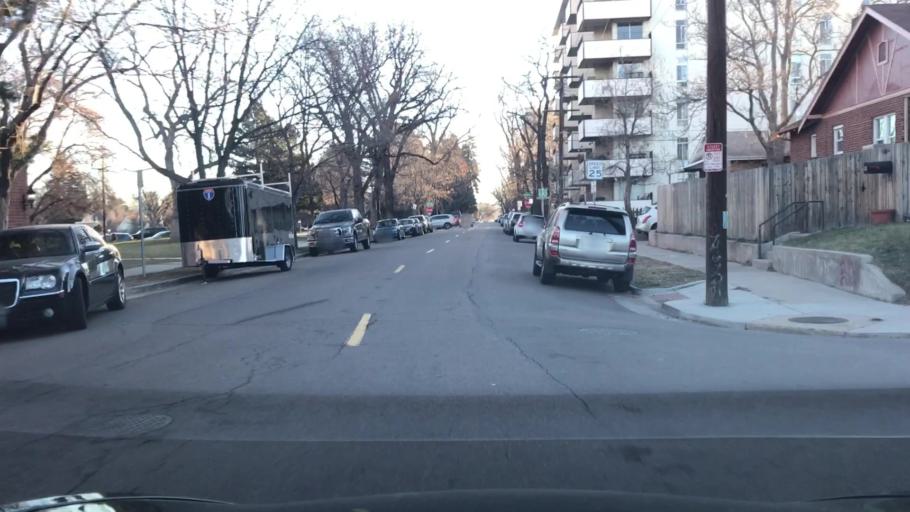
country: US
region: Colorado
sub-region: Denver County
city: Denver
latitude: 39.7183
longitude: -104.9782
